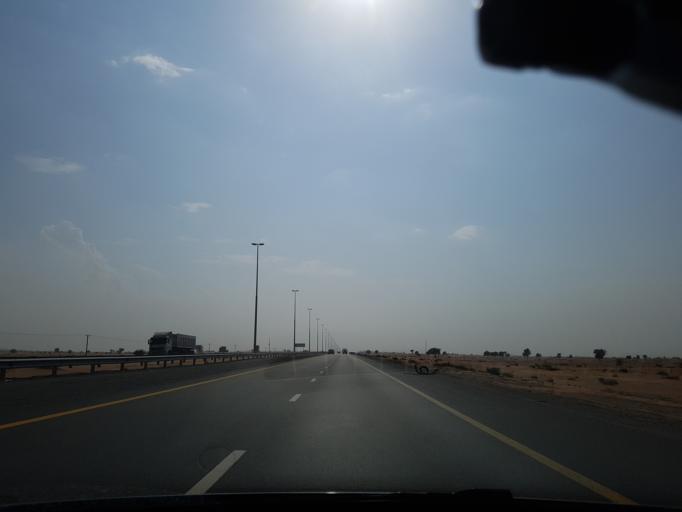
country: AE
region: Umm al Qaywayn
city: Umm al Qaywayn
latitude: 25.5356
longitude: 55.7712
